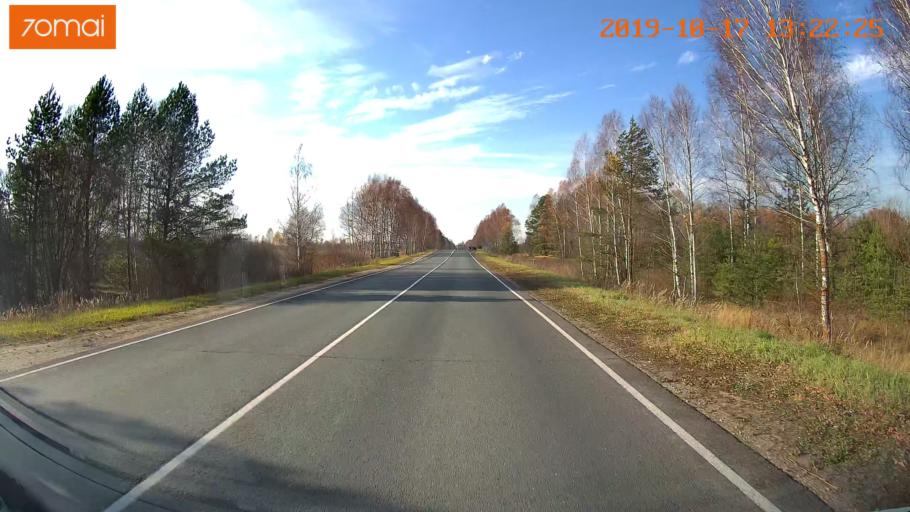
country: RU
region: Rjazan
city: Gus'-Zheleznyy
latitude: 55.0859
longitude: 41.0038
